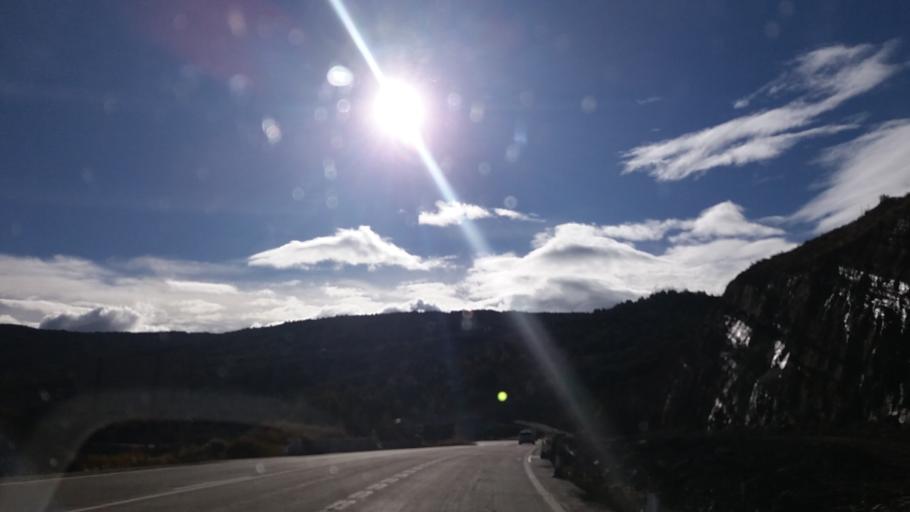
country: ES
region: Aragon
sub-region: Provincia de Huesca
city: Arguis
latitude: 42.3729
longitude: -0.3737
